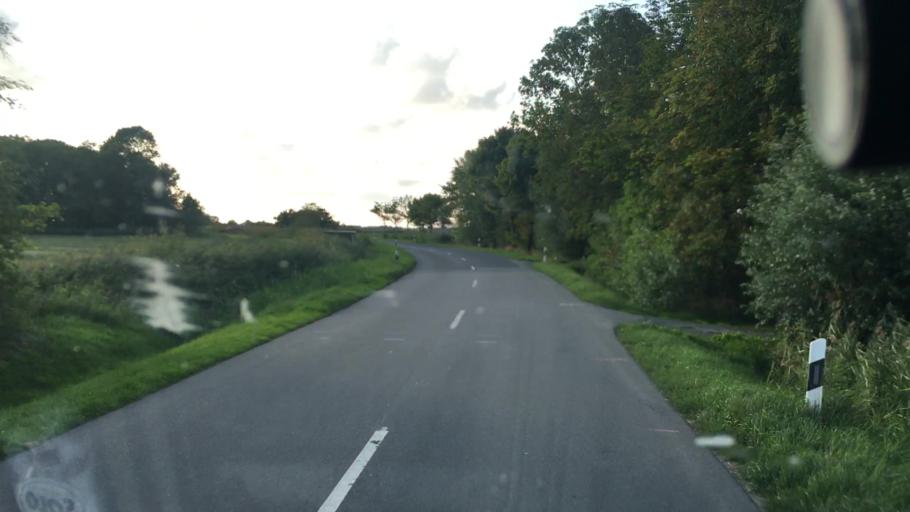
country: DE
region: Lower Saxony
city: Werdum
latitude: 53.6681
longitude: 7.7284
